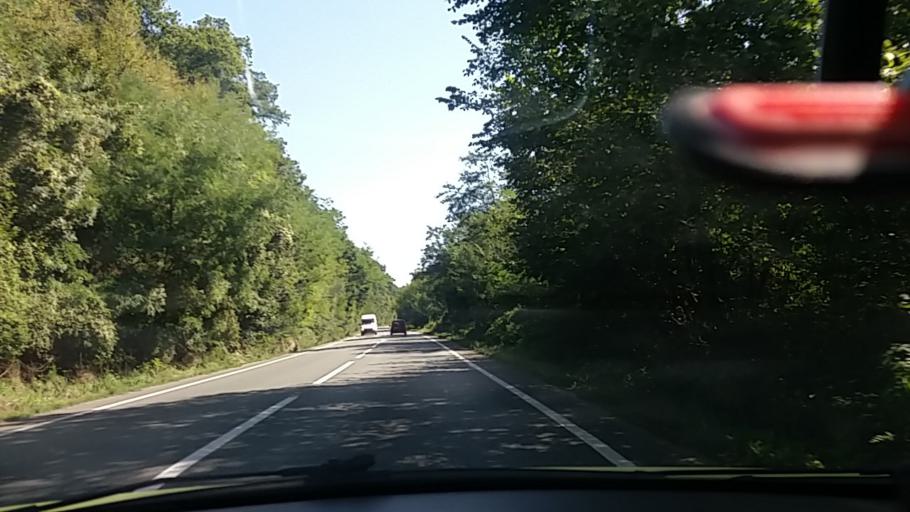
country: RO
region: Arad
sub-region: Comuna Conop
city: Conop
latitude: 46.1030
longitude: 21.9308
